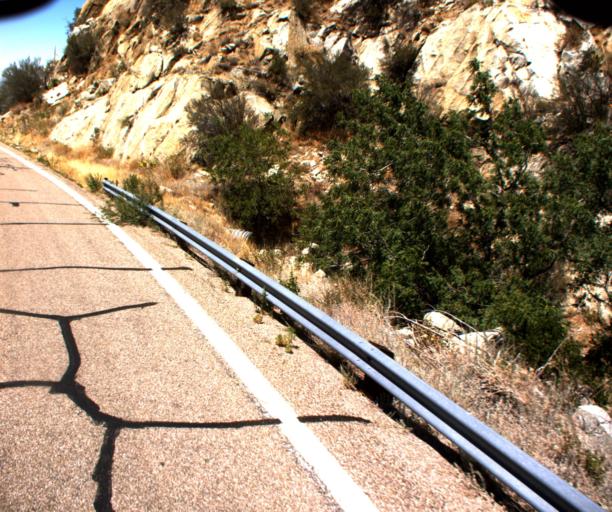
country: US
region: Arizona
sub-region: Pima County
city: Sells
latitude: 31.9690
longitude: -111.6102
